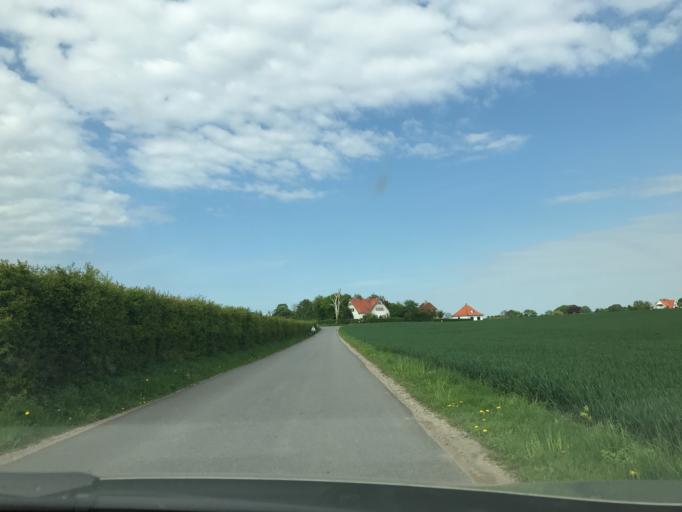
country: DK
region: South Denmark
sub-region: Middelfart Kommune
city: Norre Aby
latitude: 55.3692
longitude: 9.8420
